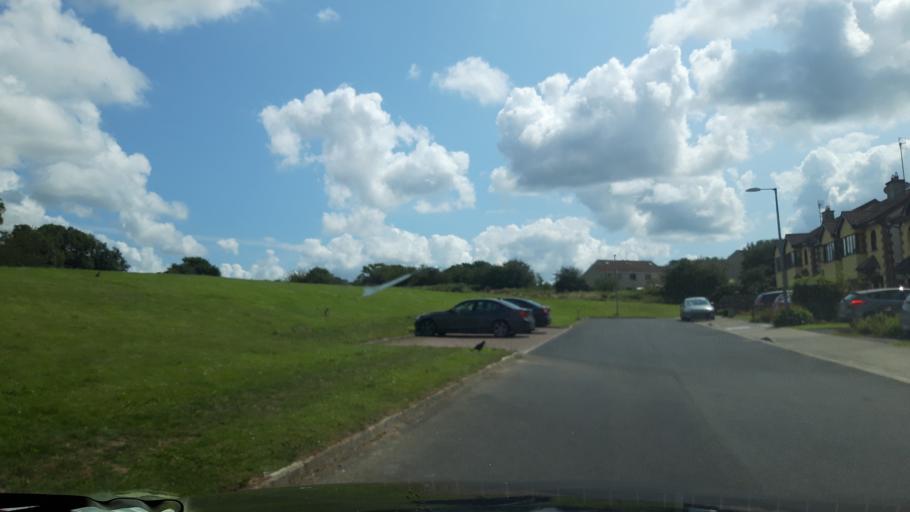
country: IE
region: Munster
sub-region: Waterford
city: Waterford
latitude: 52.2671
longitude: -7.0888
